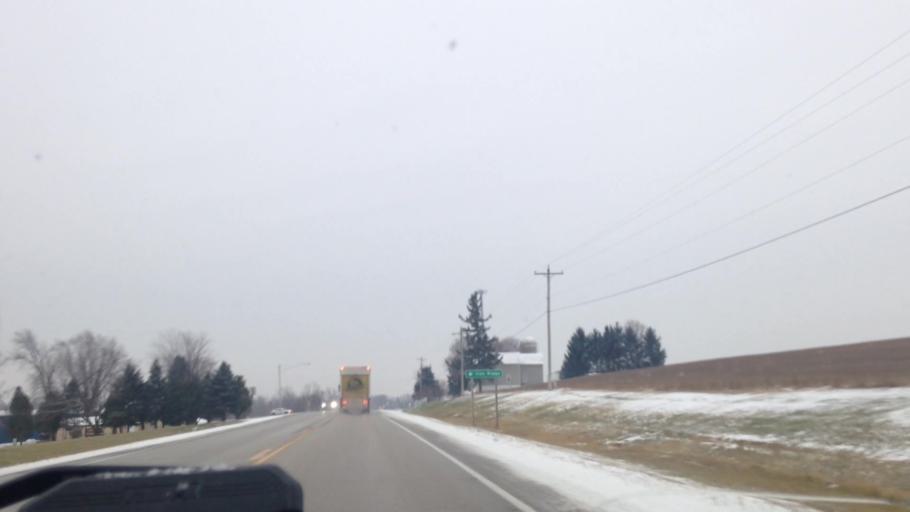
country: US
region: Wisconsin
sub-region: Dodge County
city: Hustisford
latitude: 43.4014
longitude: -88.5420
